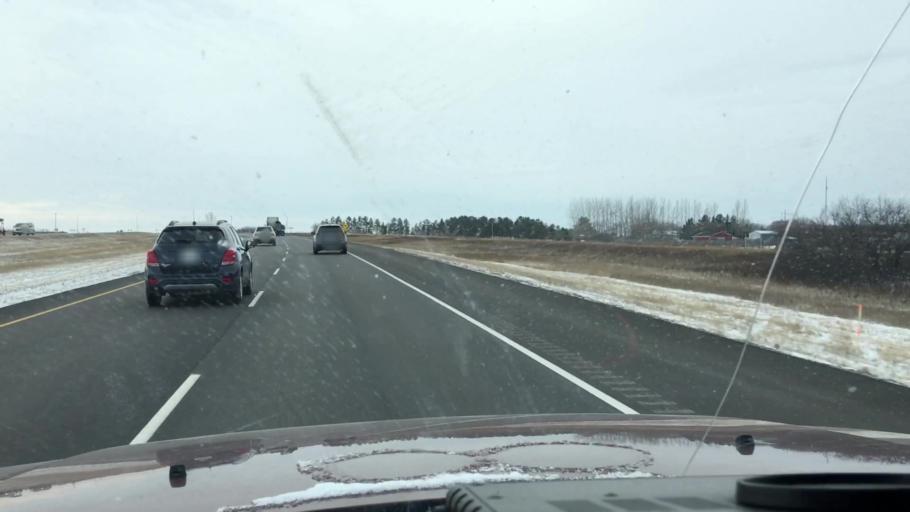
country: CA
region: Saskatchewan
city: Saskatoon
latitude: 51.8576
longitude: -106.5082
